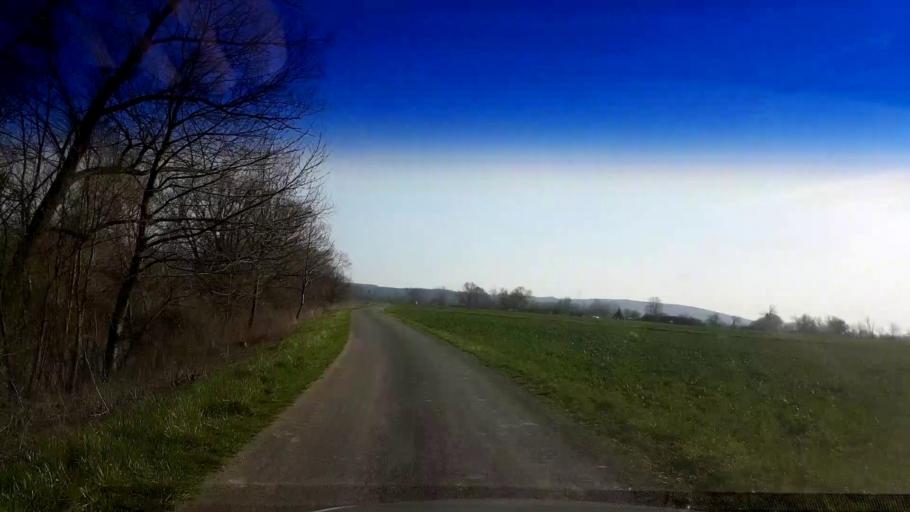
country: DE
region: Bavaria
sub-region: Upper Franconia
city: Ebensfeld
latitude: 50.0487
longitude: 10.9340
